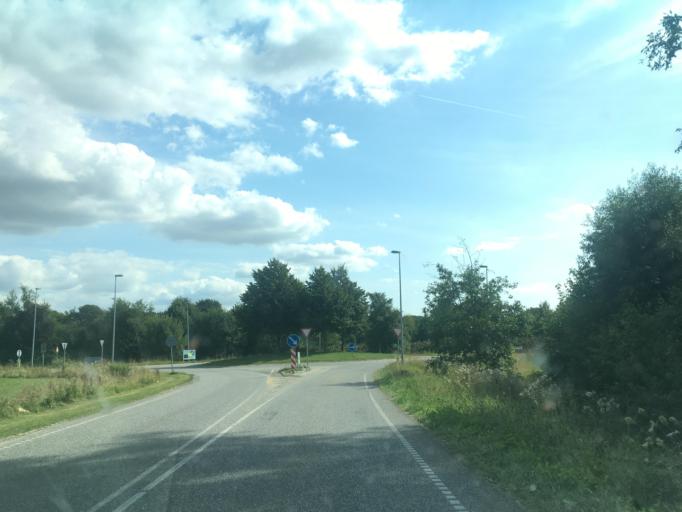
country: DK
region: South Denmark
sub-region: Middelfart Kommune
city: Ejby
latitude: 55.3934
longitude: 9.9639
